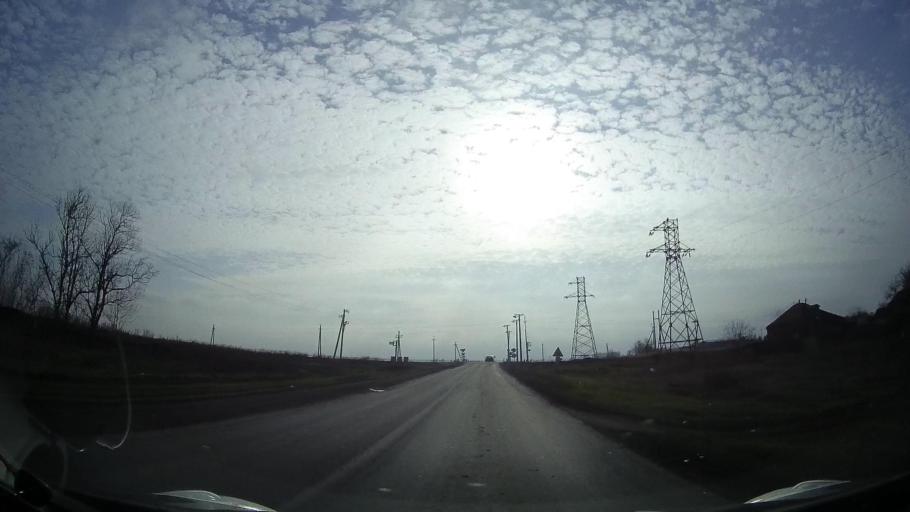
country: RU
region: Rostov
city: Mechetinskaya
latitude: 46.7865
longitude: 40.4835
